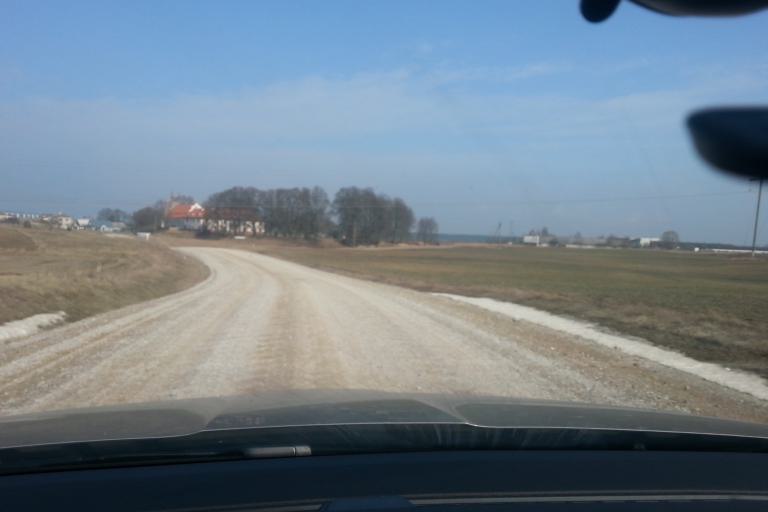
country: LT
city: Trakai
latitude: 54.6021
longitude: 24.9825
